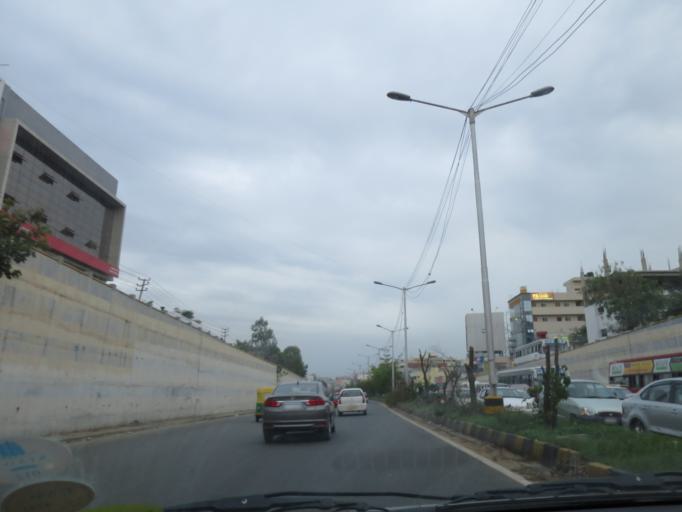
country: IN
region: Karnataka
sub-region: Bangalore Urban
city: Bangalore
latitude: 12.9562
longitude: 77.7010
